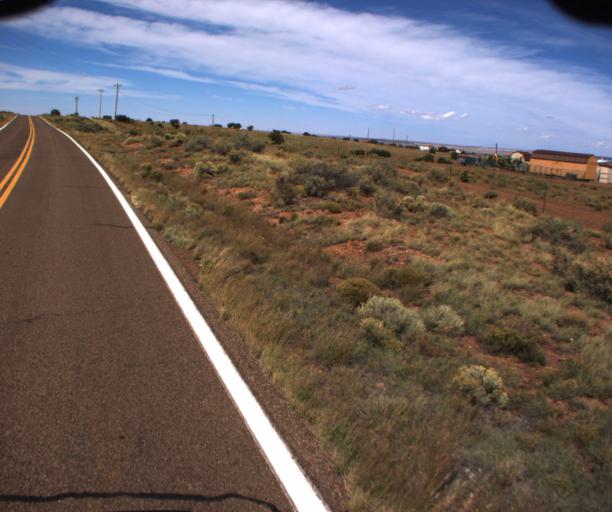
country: US
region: Arizona
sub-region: Apache County
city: Saint Johns
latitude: 34.5548
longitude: -109.6256
